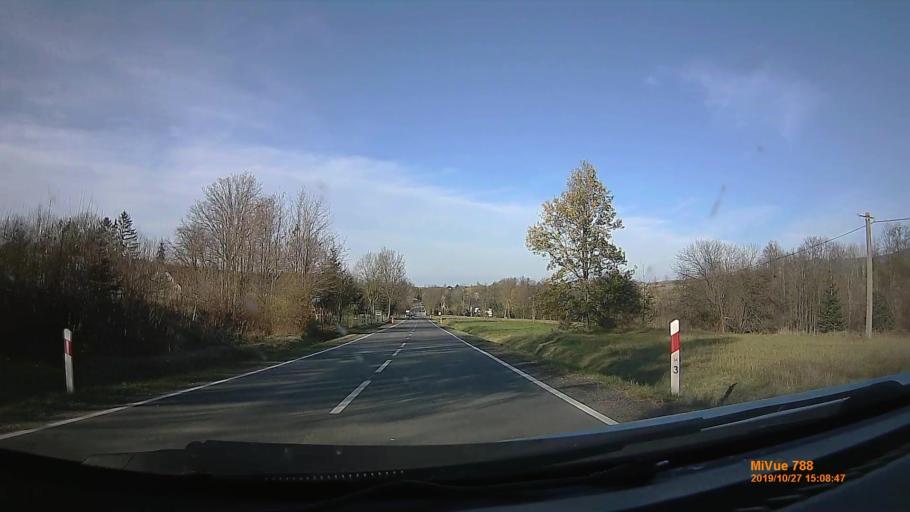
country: PL
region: Lower Silesian Voivodeship
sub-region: Powiat klodzki
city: Miedzylesie
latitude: 50.1738
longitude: 16.6698
